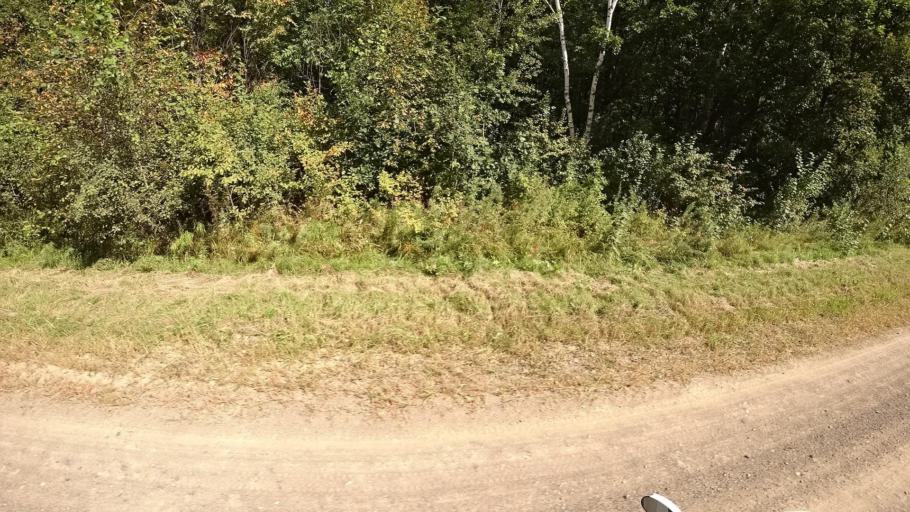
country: RU
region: Primorskiy
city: Yakovlevka
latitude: 44.7010
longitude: 133.6435
